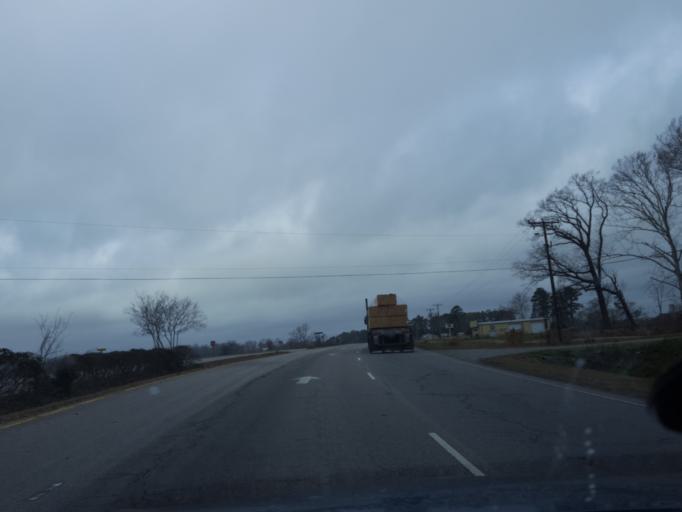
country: US
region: North Carolina
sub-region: Washington County
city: Plymouth
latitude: 35.8289
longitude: -76.7875
